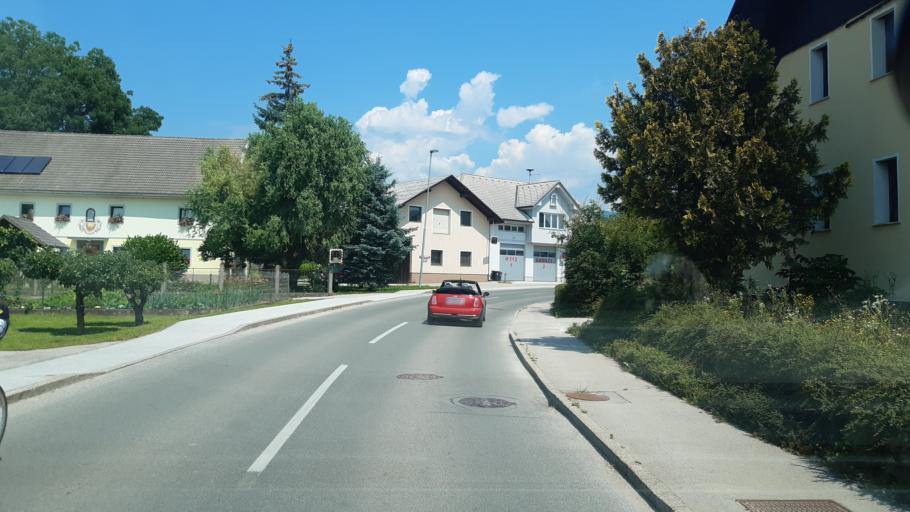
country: SI
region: Cerklje na Gorenjskem
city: Cerklje na Gorenjskem
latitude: 46.2404
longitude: 14.4845
